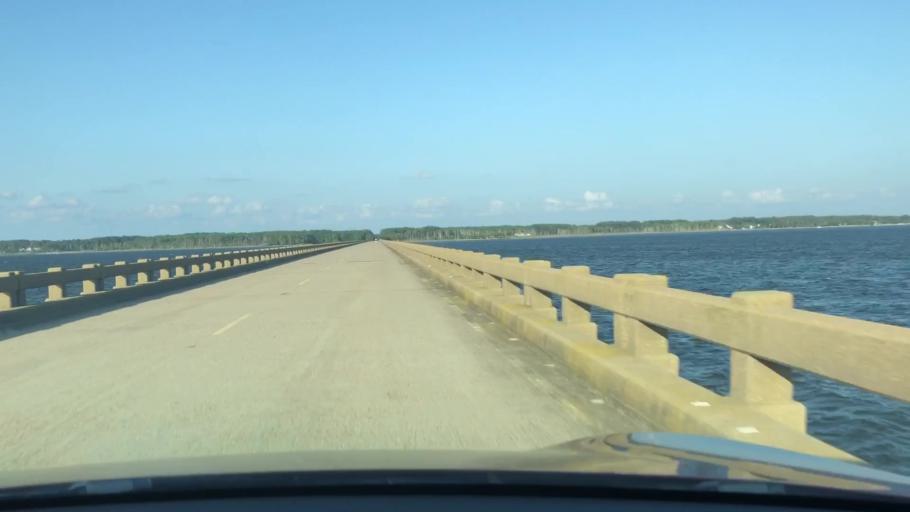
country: US
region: North Carolina
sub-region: Dare County
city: Manteo
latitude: 35.9249
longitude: -75.7367
